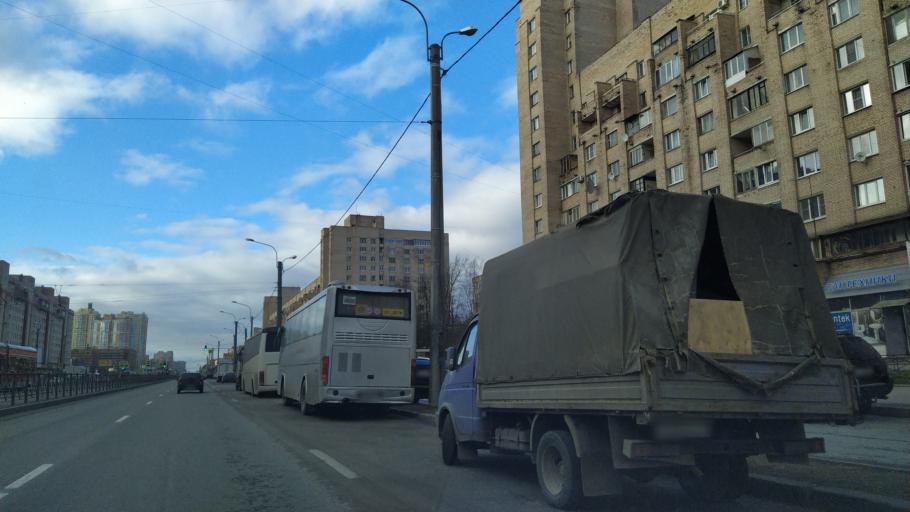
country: RU
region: St.-Petersburg
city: Grazhdanka
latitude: 60.0431
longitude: 30.3836
